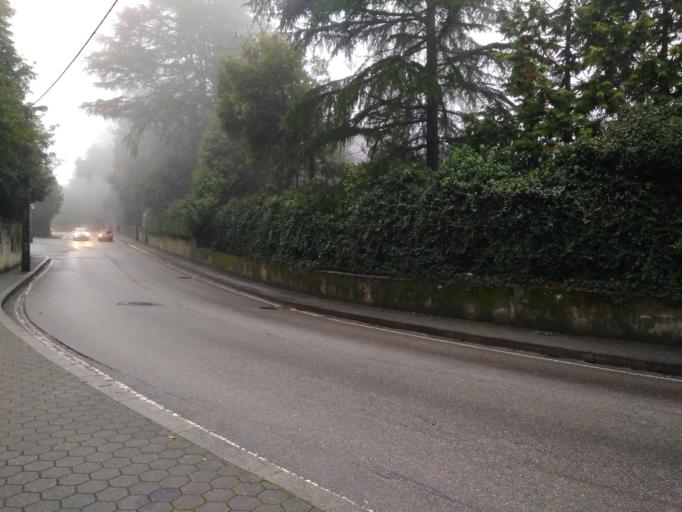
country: PT
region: Porto
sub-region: Vila Nova de Gaia
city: Vilar de Andorinho
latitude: 41.1104
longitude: -8.6035
